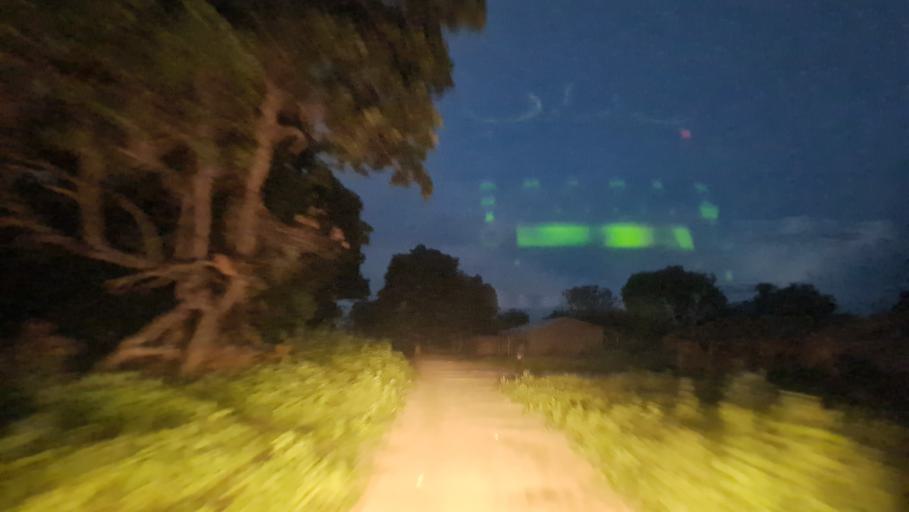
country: MZ
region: Nampula
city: Nampula
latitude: -14.6677
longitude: 39.8362
